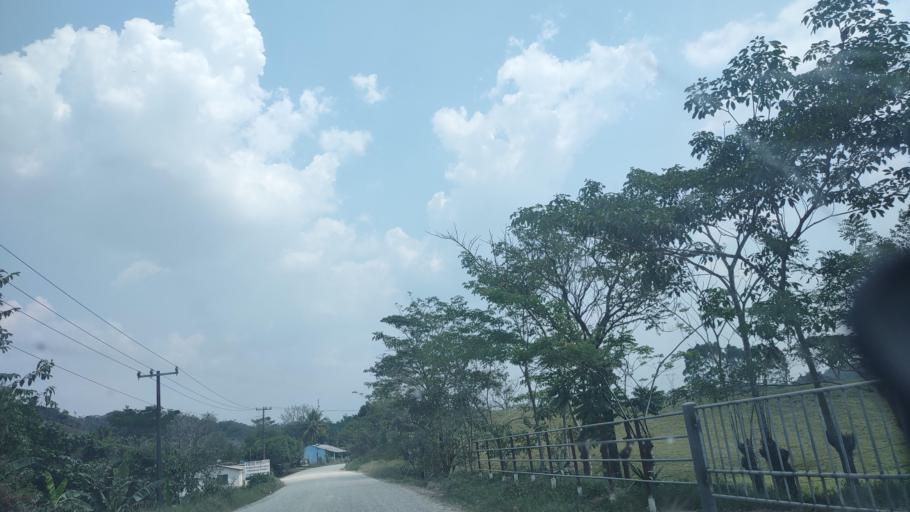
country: MX
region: Tabasco
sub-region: Huimanguillo
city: Francisco Rueda
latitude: 17.6014
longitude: -93.9007
